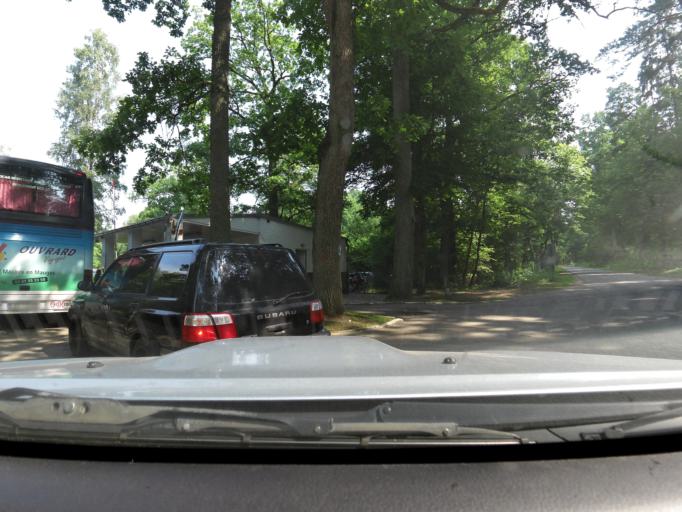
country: PL
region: Warmian-Masurian Voivodeship
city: Gierloz
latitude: 54.0789
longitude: 21.4932
